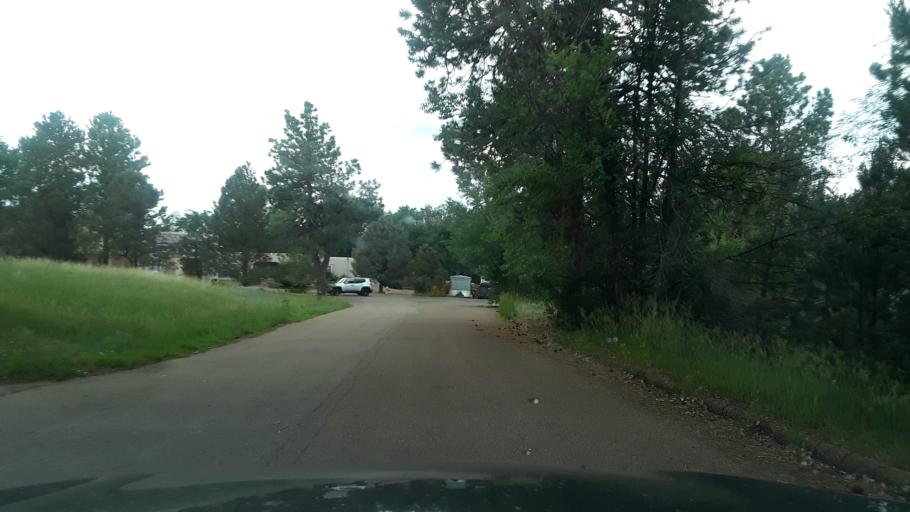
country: US
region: Colorado
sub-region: El Paso County
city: Air Force Academy
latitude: 38.9448
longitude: -104.8225
